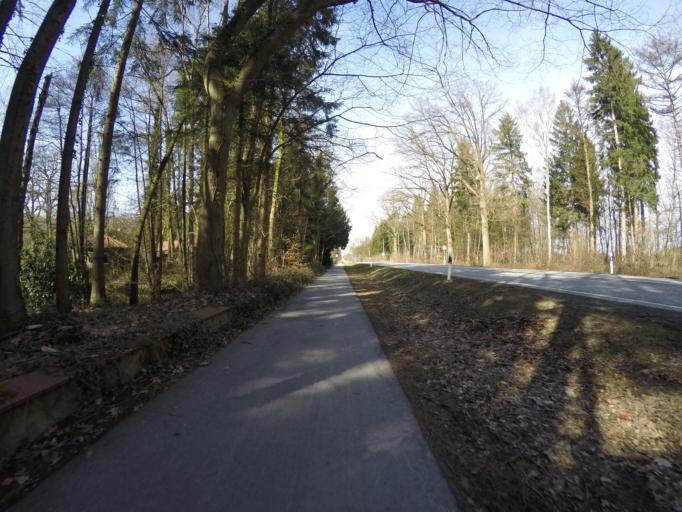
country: DE
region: Schleswig-Holstein
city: Bilsen
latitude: 53.7542
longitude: 9.8828
